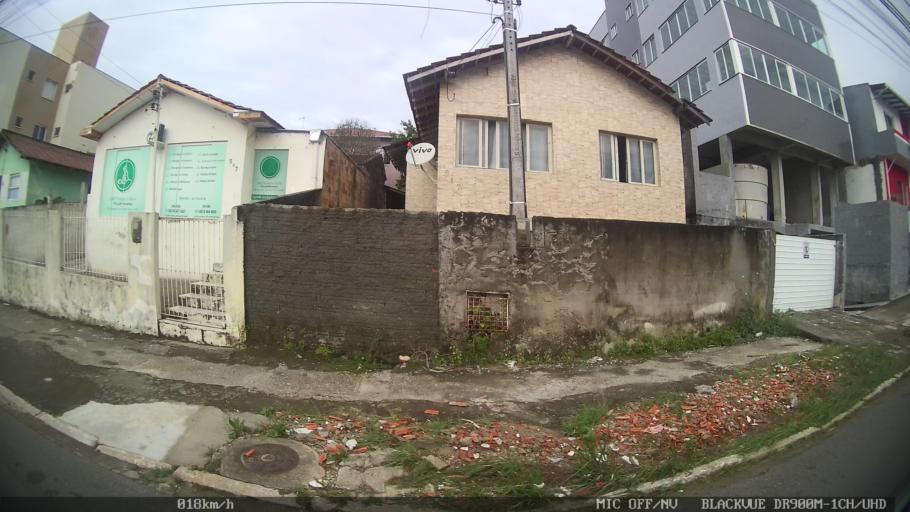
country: BR
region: Santa Catarina
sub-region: Sao Jose
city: Campinas
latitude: -27.5707
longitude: -48.6178
